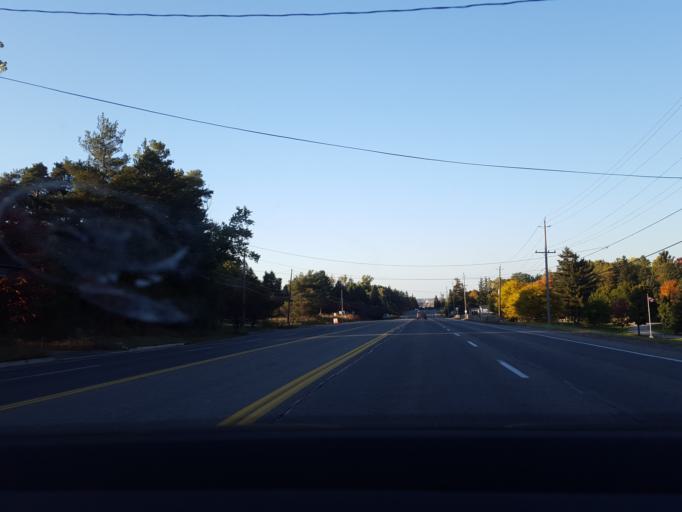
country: CA
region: Ontario
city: Newmarket
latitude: 43.9729
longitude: -79.4612
